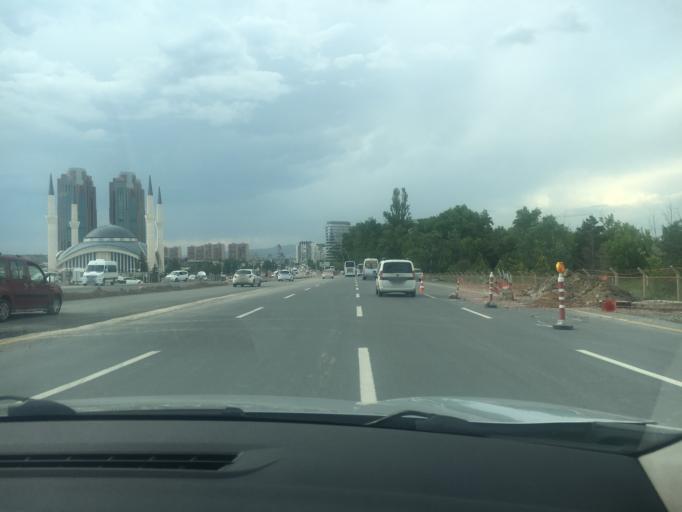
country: TR
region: Ankara
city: Batikent
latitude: 39.9031
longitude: 32.7655
